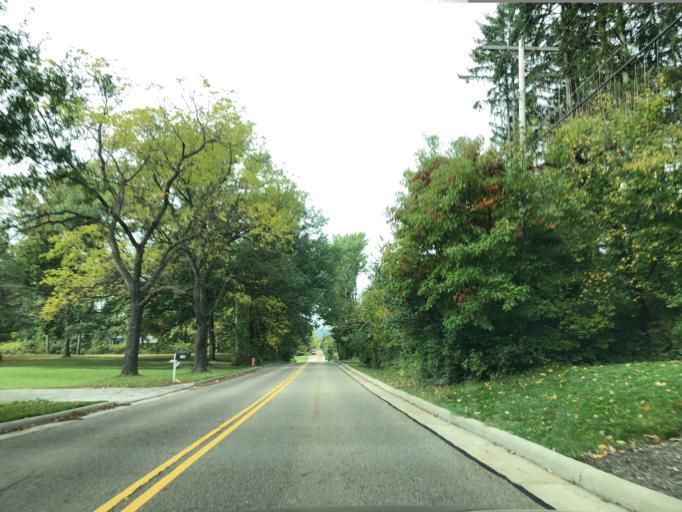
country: US
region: Ohio
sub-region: Summit County
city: Boston Heights
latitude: 41.2632
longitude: -81.5161
